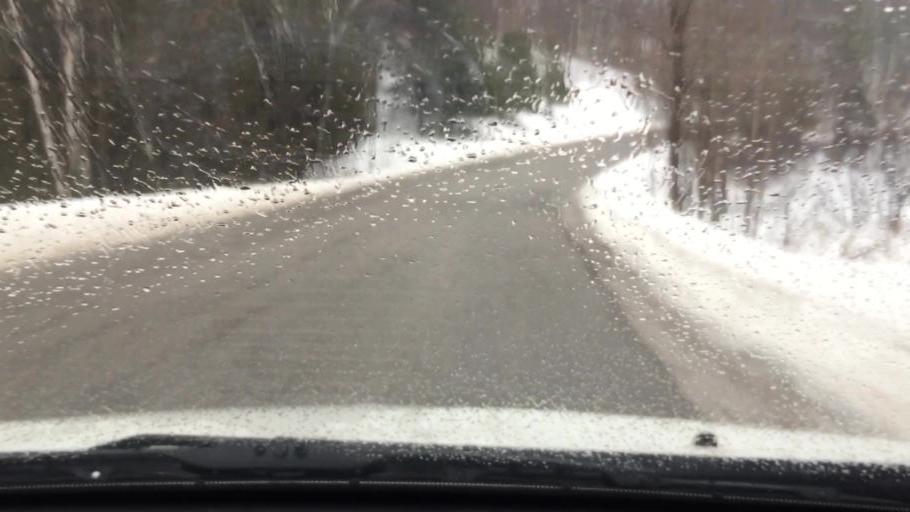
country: US
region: Michigan
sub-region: Charlevoix County
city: East Jordan
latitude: 45.1055
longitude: -85.1474
